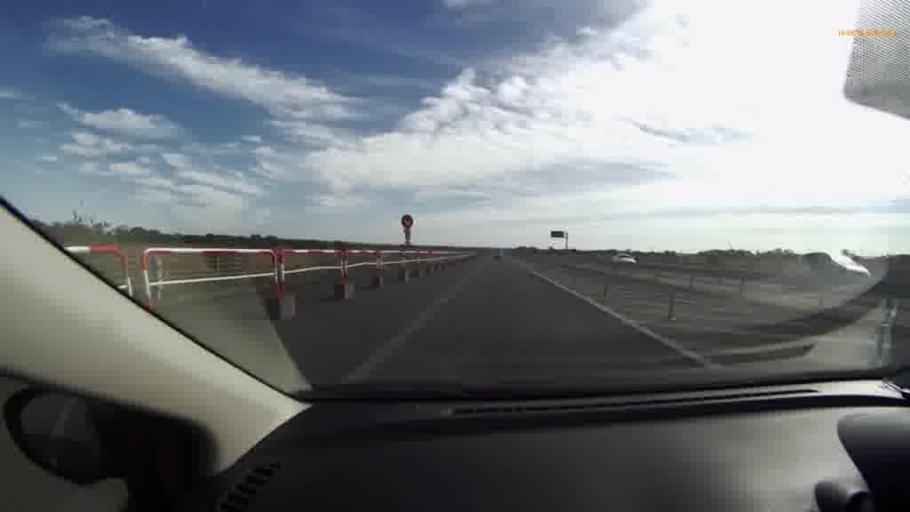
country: JP
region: Hokkaido
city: Kushiro
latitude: 43.0374
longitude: 144.3343
